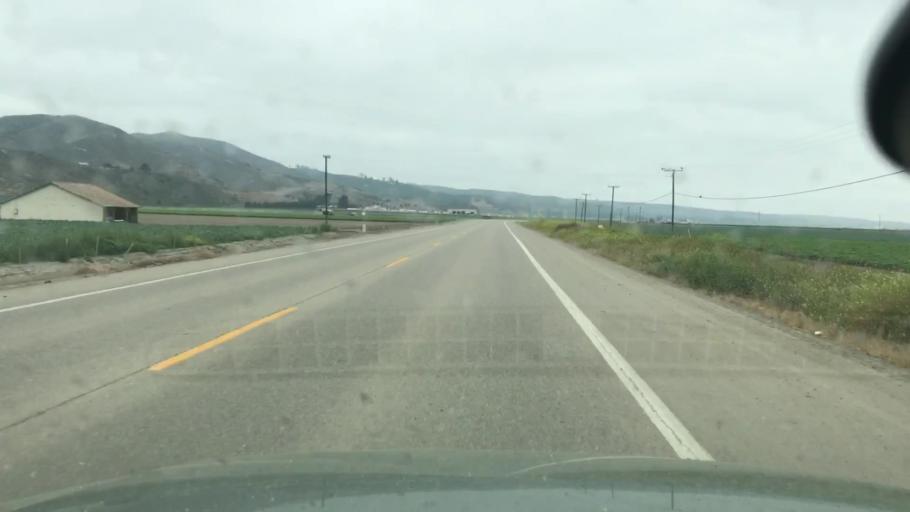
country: US
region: California
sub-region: Santa Barbara County
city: Lompoc
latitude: 34.6392
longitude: -120.4855
